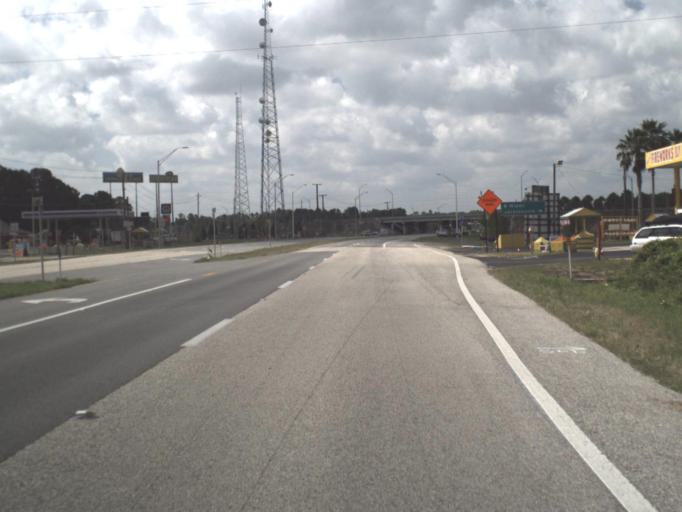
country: US
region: Florida
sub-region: Flagler County
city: Palm Coast
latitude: 29.6657
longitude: -81.2883
